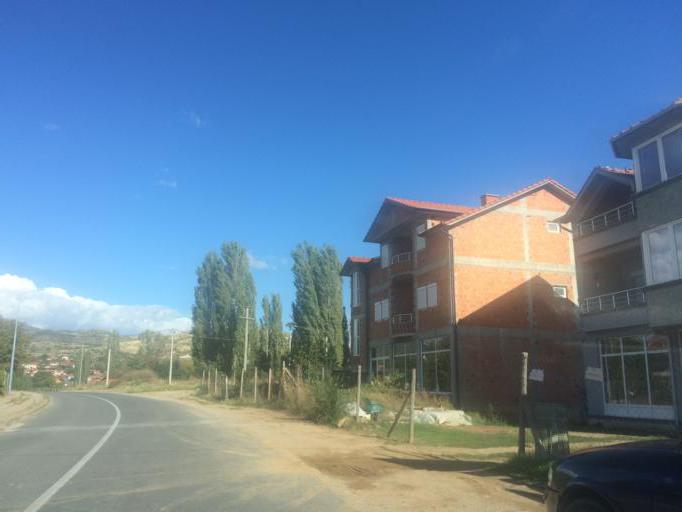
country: MK
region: Kocani
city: Orizari
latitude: 41.9150
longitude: 22.4414
